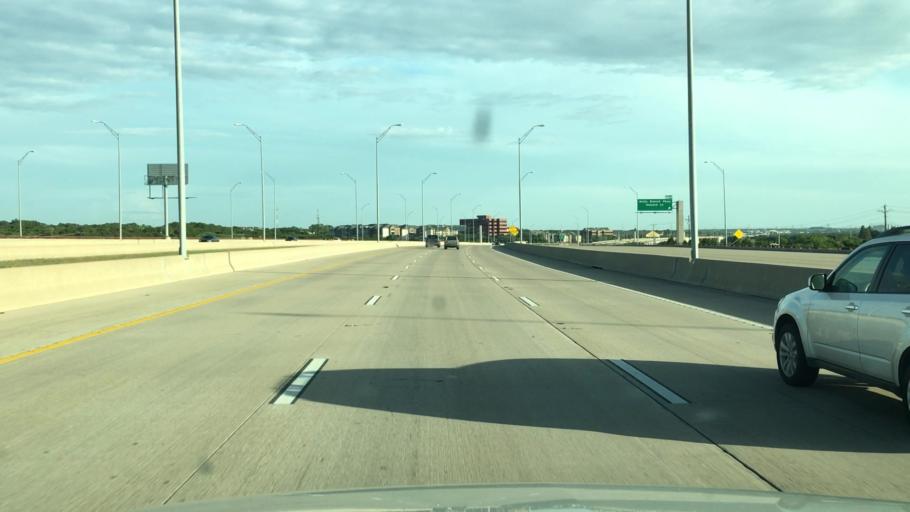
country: US
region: Texas
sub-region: Travis County
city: Wells Branch
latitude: 30.4523
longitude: -97.6968
